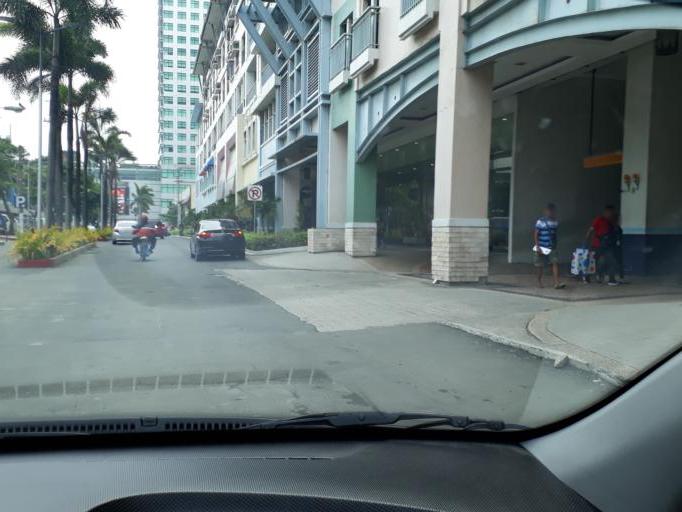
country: PH
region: Metro Manila
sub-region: Quezon City
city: Quezon City
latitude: 14.6218
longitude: 121.0557
